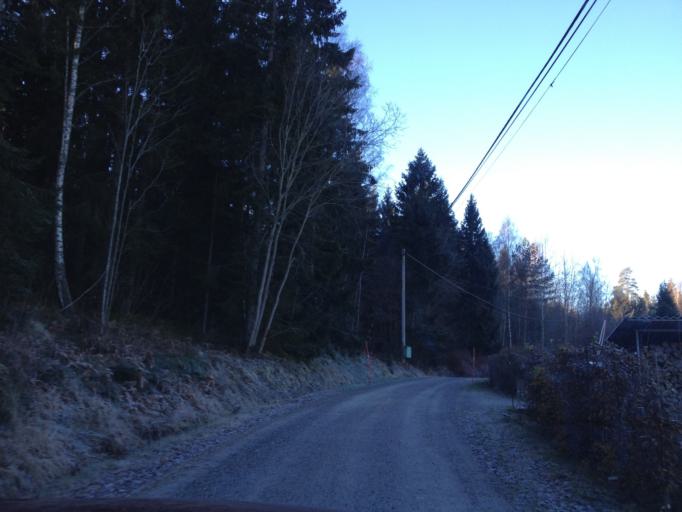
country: SE
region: Stockholm
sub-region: Sodertalje Kommun
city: Soedertaelje
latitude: 59.1625
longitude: 17.5804
